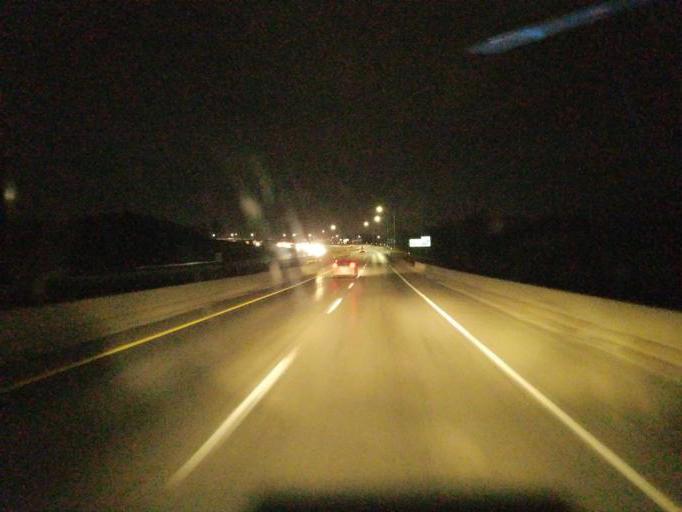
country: US
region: Iowa
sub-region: Dallas County
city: Waukee
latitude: 41.5651
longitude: -93.8645
